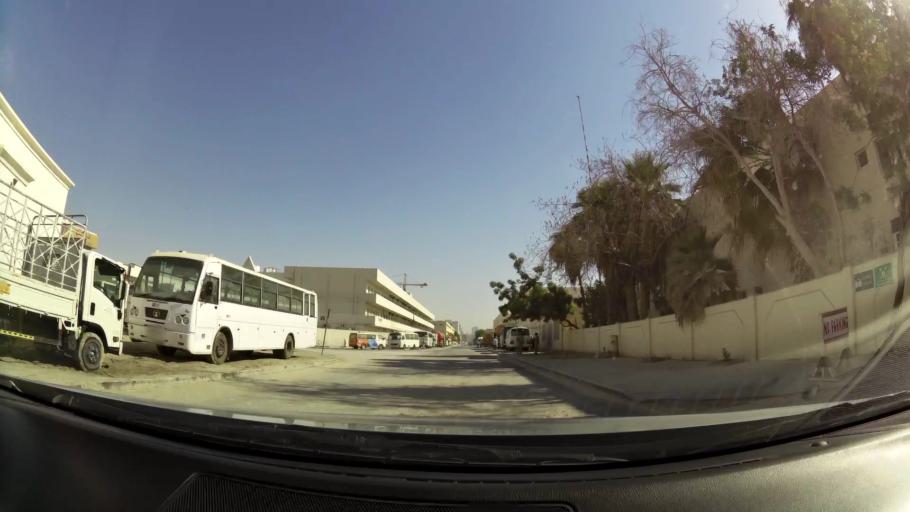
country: AE
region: Dubai
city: Dubai
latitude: 25.0098
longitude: 55.1035
